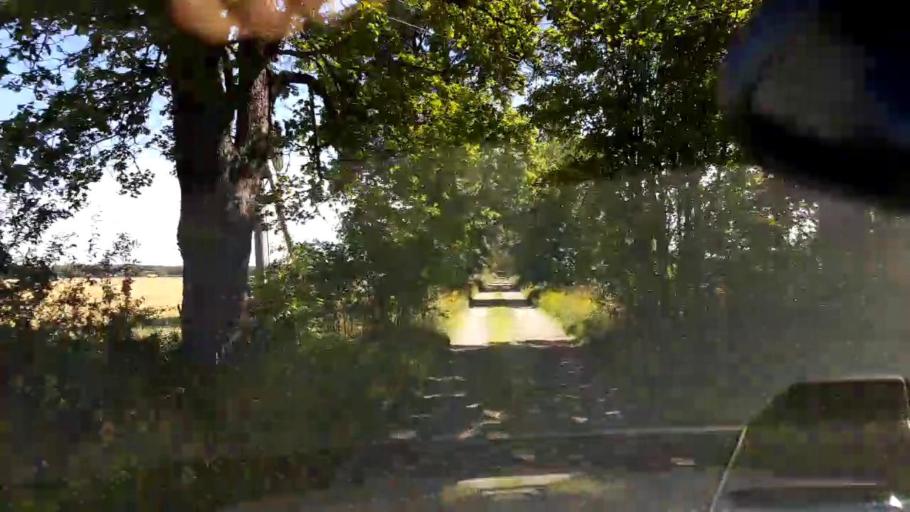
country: SE
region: Stockholm
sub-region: Upplands-Bro Kommun
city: Bro
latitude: 59.5867
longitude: 17.6298
